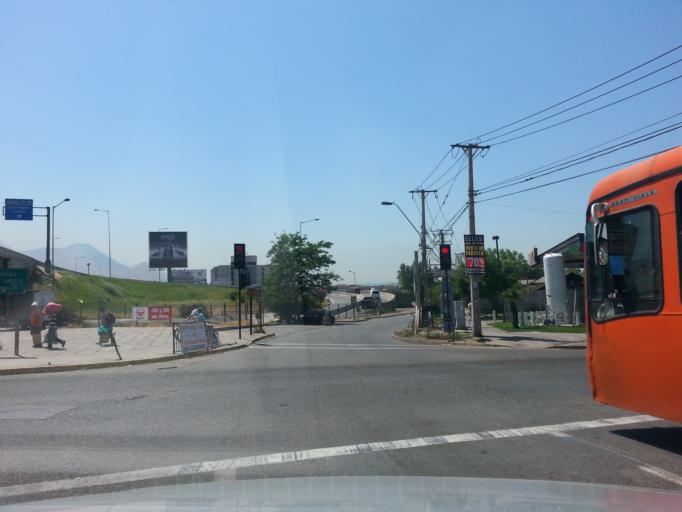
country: CL
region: Santiago Metropolitan
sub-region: Provincia de Santiago
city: Lo Prado
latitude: -33.3665
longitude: -70.6894
